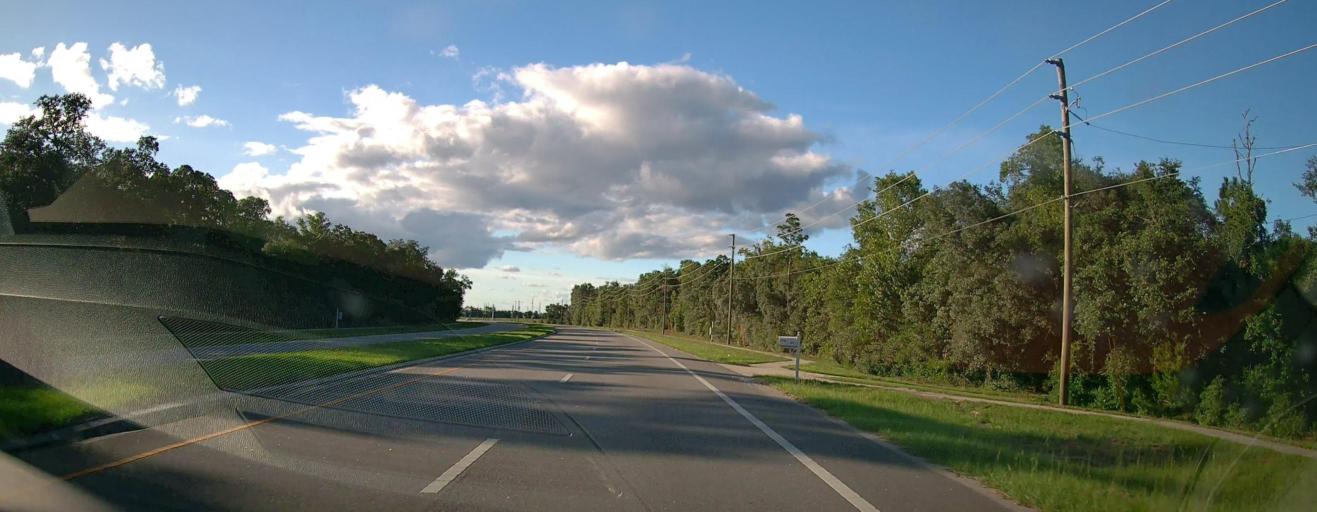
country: US
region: Florida
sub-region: Marion County
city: Silver Springs Shores
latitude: 29.0592
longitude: -82.0165
